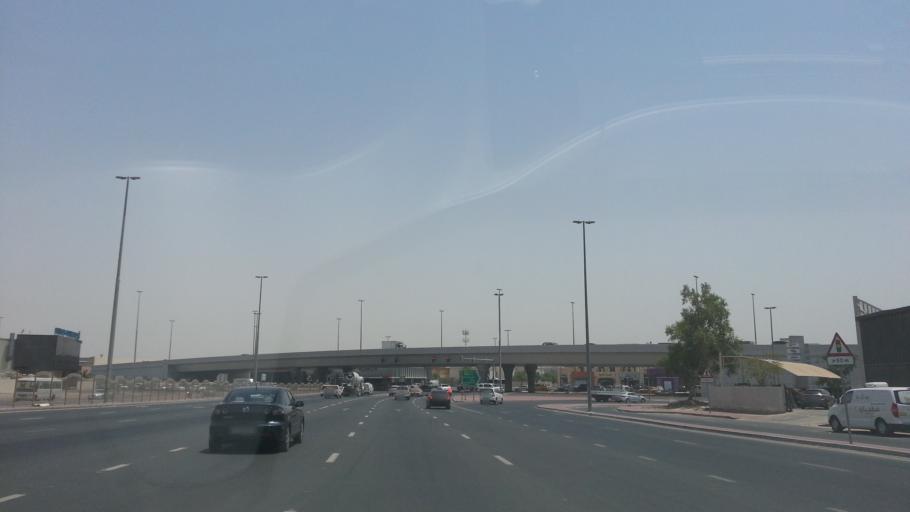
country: AE
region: Dubai
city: Dubai
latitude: 25.1128
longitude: 55.2197
